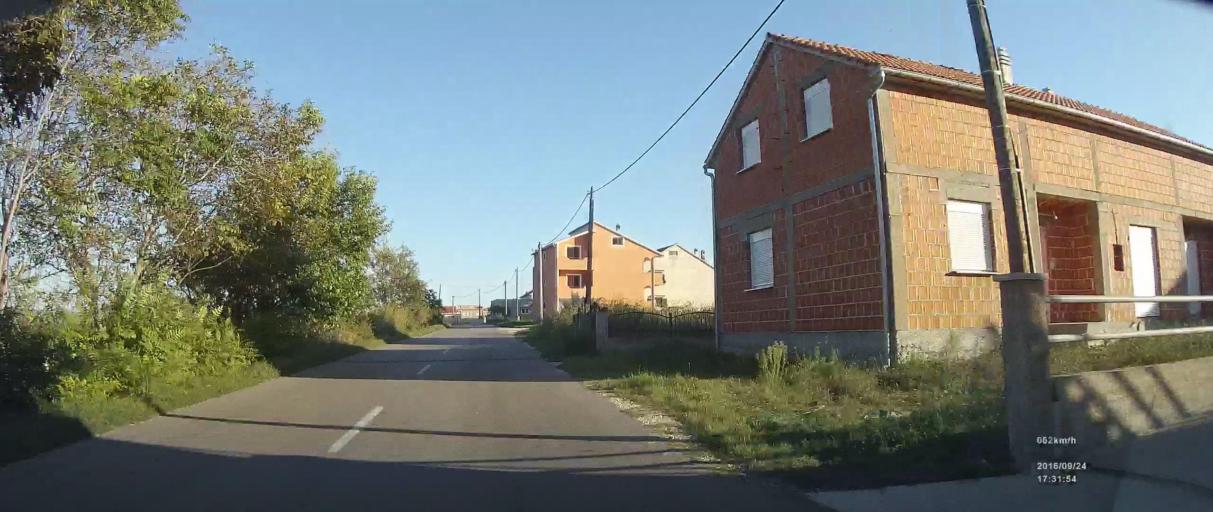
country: HR
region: Zadarska
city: Posedarje
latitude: 44.1858
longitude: 15.4460
